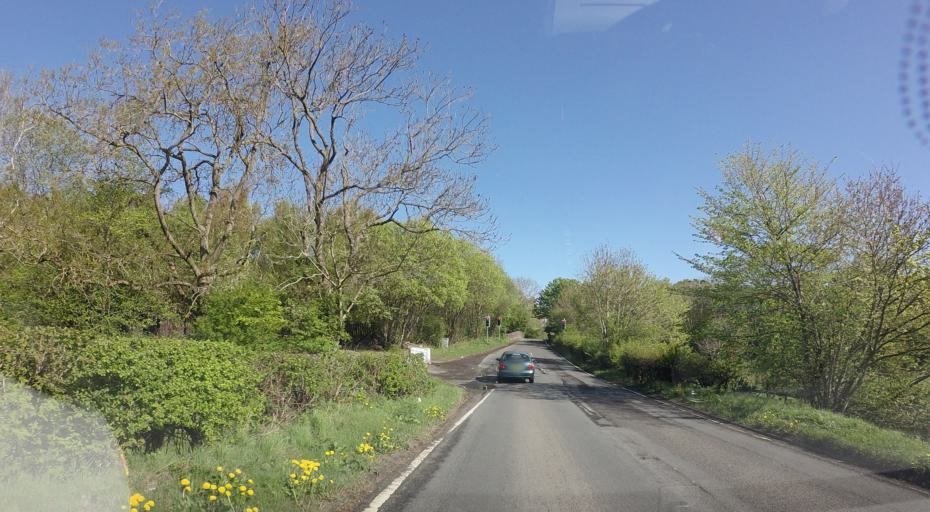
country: GB
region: Scotland
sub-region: West Lothian
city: Broxburn
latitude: 55.9734
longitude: -3.5087
